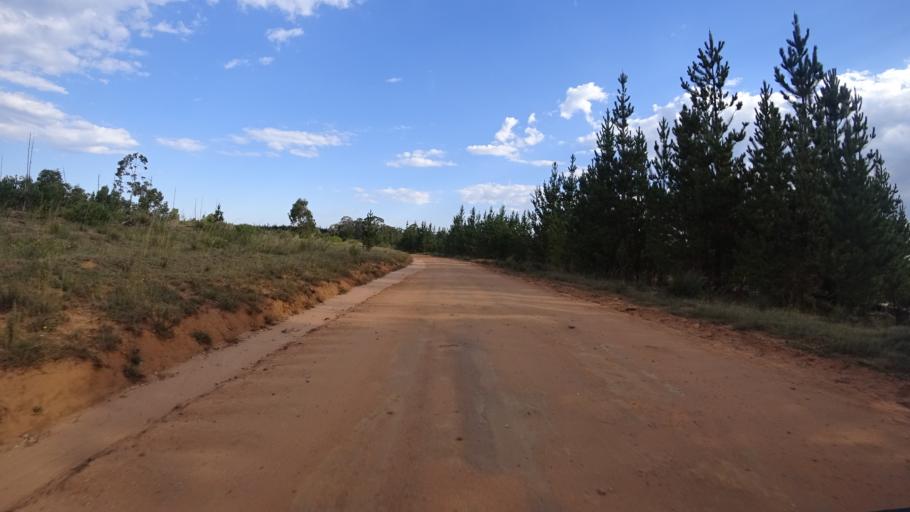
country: AU
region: New South Wales
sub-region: Lithgow
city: Lithgow
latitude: -33.3538
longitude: 150.2527
